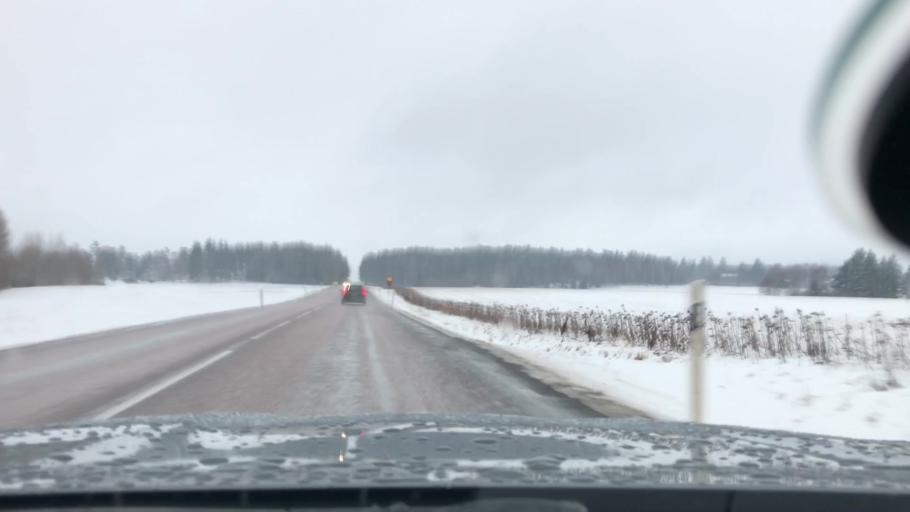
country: SE
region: Stockholm
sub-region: Sodertalje Kommun
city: Pershagen
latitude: 59.0487
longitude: 17.6071
